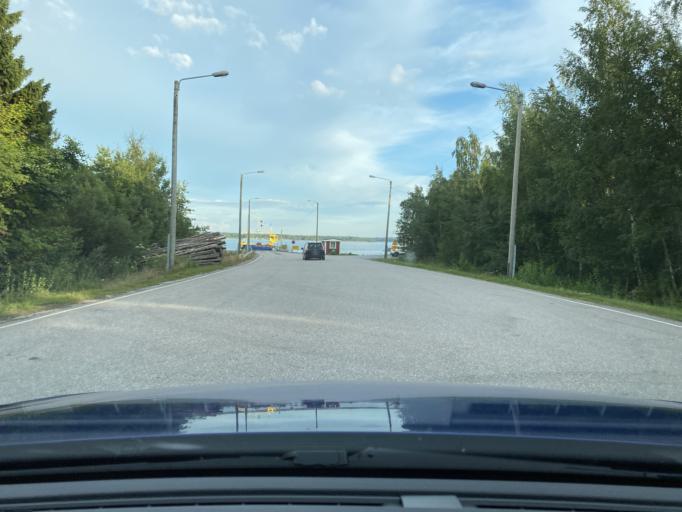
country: FI
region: Ostrobothnia
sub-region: Vaasa
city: Korsnaes
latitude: 62.9449
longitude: 21.1760
